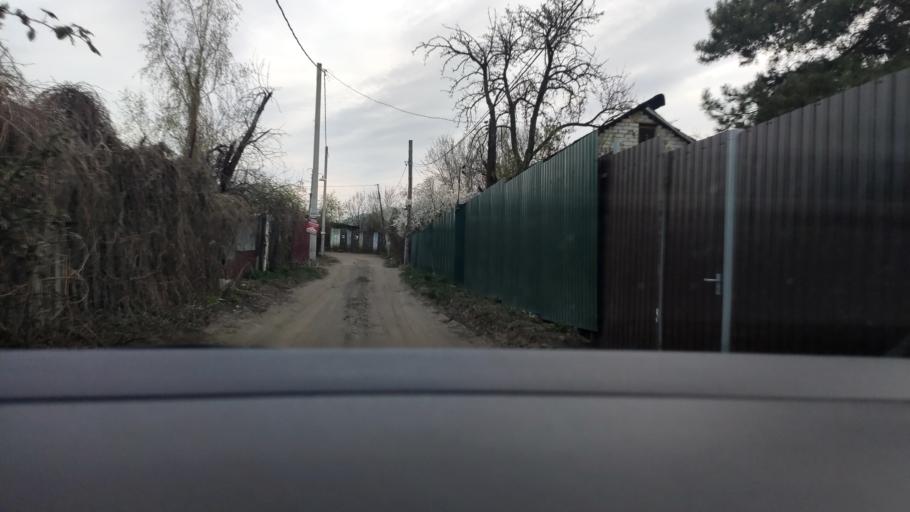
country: RU
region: Voronezj
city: Maslovka
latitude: 51.5982
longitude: 39.2310
